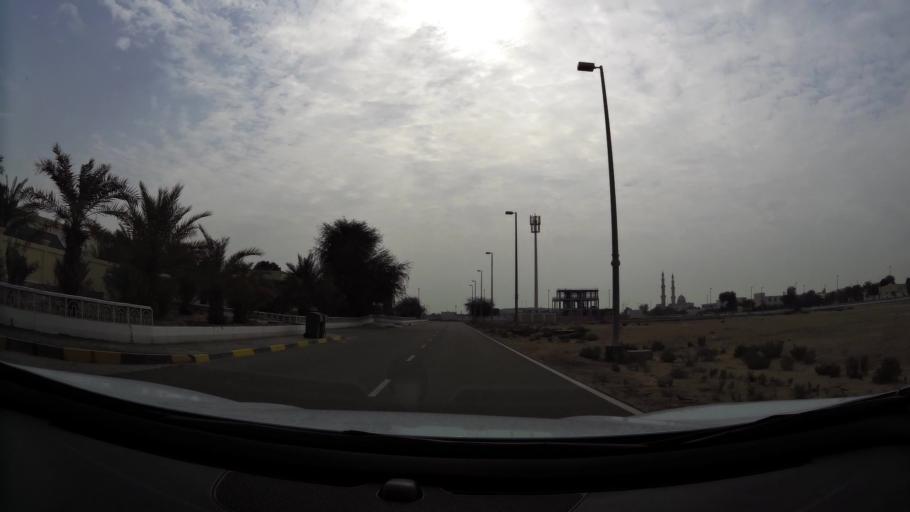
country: AE
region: Abu Dhabi
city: Abu Dhabi
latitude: 24.6770
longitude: 54.7570
